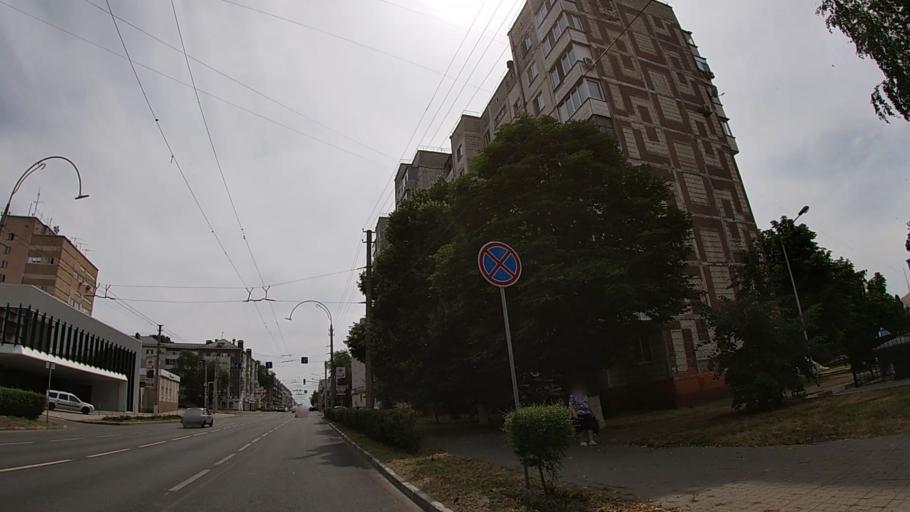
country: RU
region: Belgorod
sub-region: Belgorodskiy Rayon
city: Belgorod
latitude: 50.5989
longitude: 36.5785
